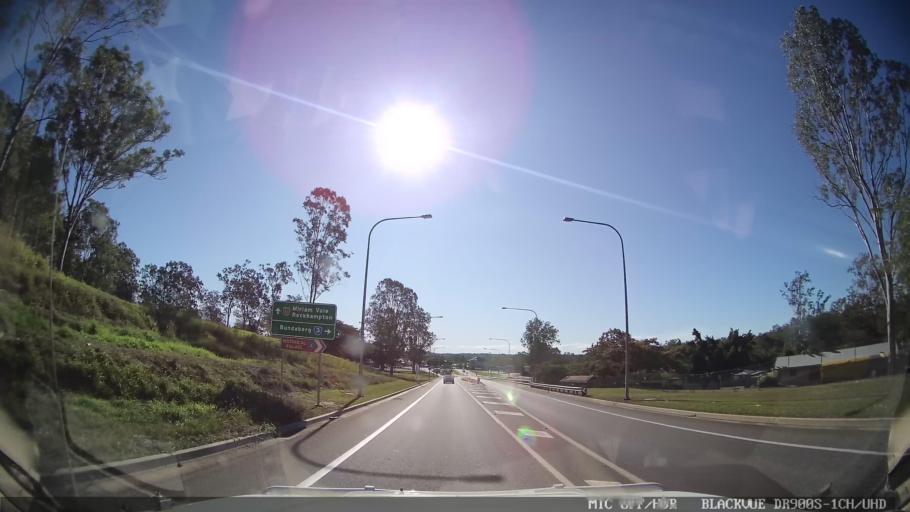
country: AU
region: Queensland
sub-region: Bundaberg
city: Sharon
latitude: -24.9950
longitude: 151.9598
